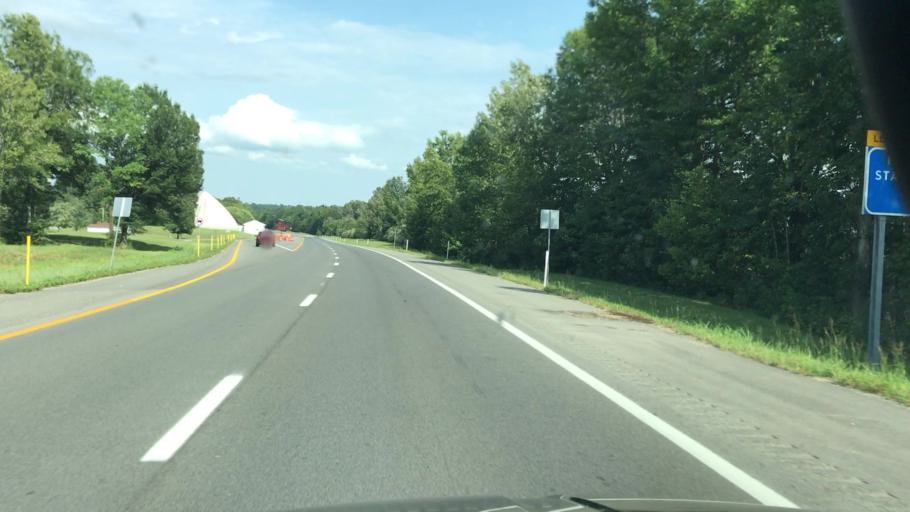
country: US
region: Kentucky
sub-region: Hopkins County
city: Nortonville
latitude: 37.2106
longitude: -87.4198
